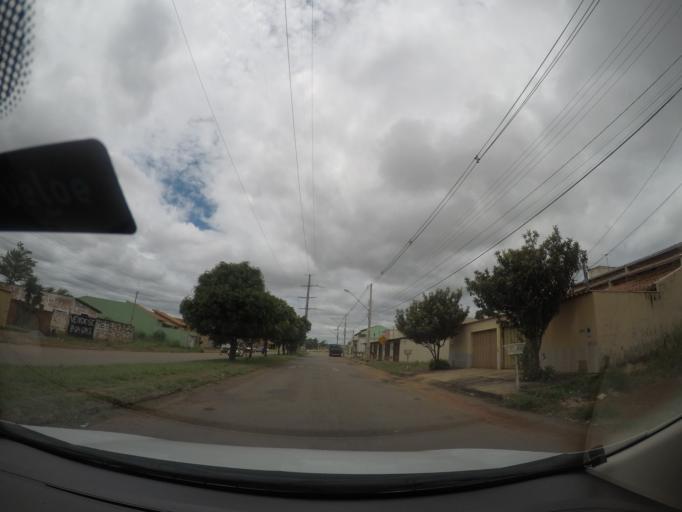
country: BR
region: Goias
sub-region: Goiania
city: Goiania
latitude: -16.7332
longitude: -49.3588
